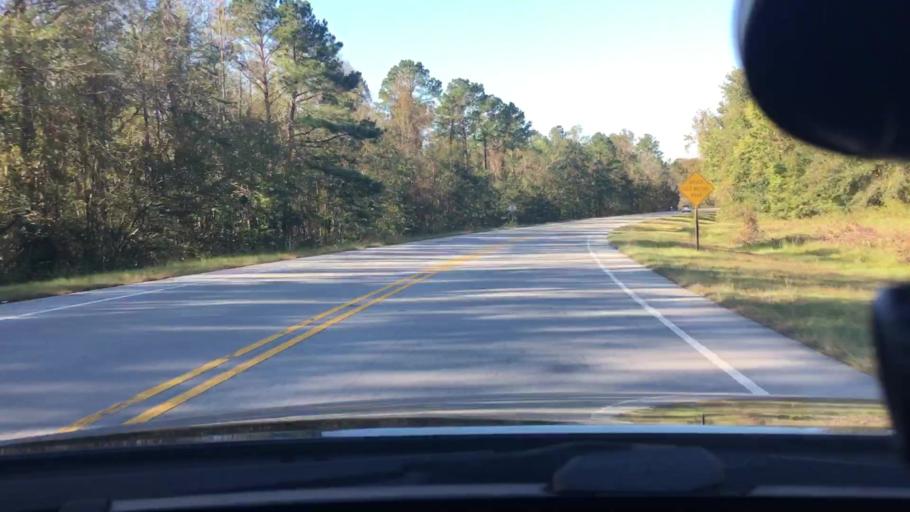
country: US
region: North Carolina
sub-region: Craven County
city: Trent Woods
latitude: 35.1755
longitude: -77.1315
